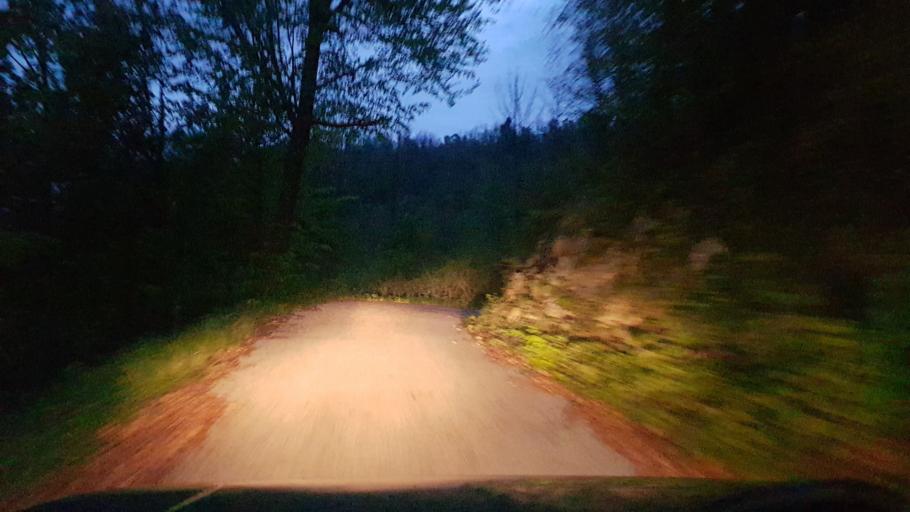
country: IT
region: Friuli Venezia Giulia
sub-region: Provincia di Udine
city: Taipana
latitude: 46.2548
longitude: 13.3547
